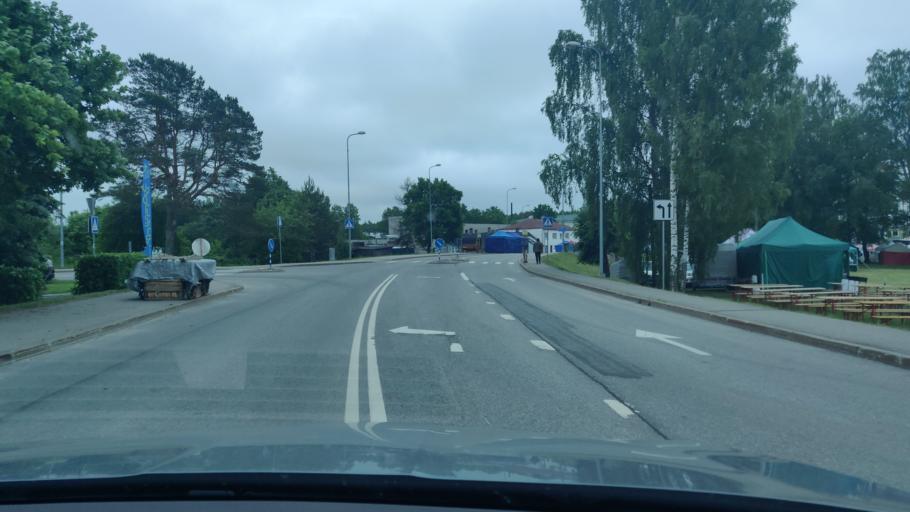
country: EE
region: Vorumaa
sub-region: Voru linn
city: Voru
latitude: 57.7339
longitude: 27.2833
